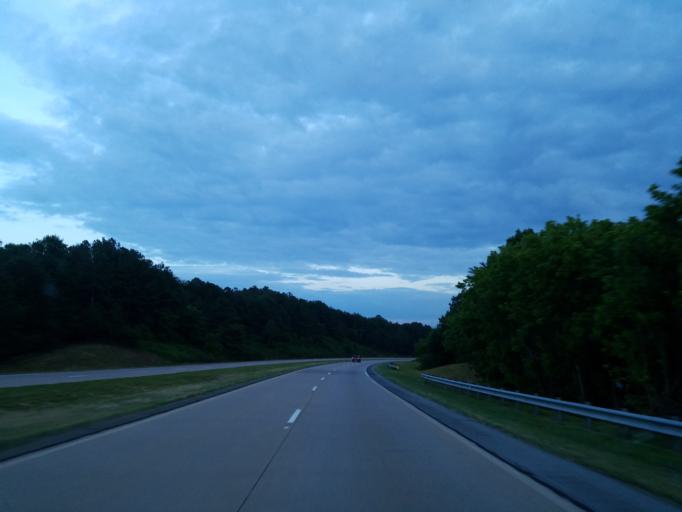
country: US
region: Georgia
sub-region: Pickens County
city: Jasper
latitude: 34.5401
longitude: -84.5164
